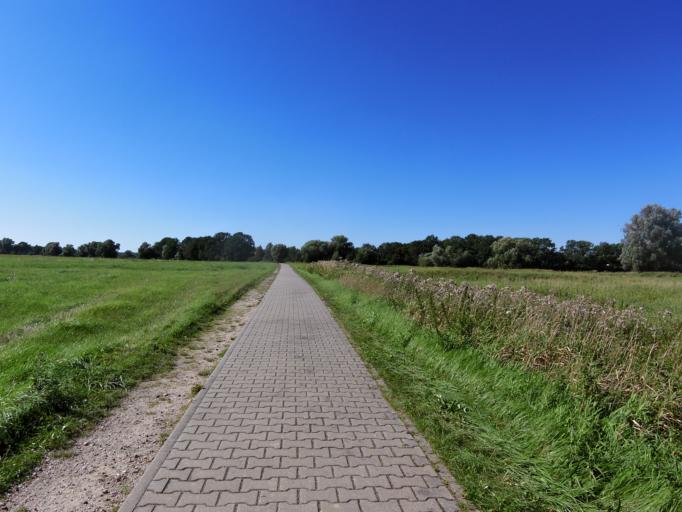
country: DE
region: Saxony-Anhalt
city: Muhlanger
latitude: 51.8501
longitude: 12.7324
